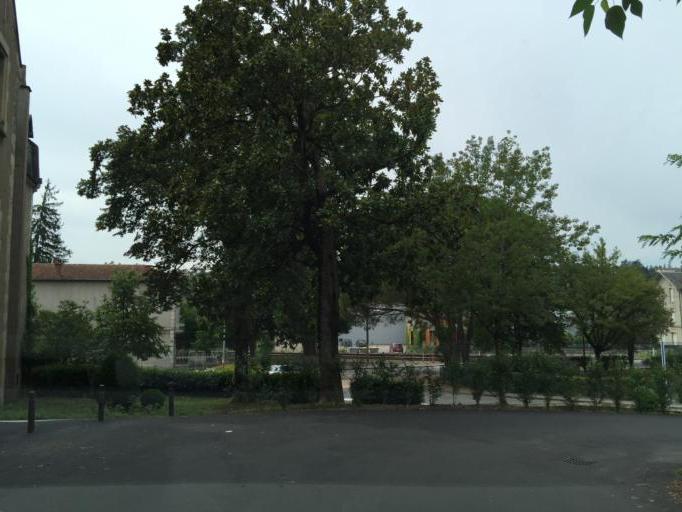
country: FR
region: Midi-Pyrenees
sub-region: Departement de l'Aveyron
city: Villefranche-de-Rouergue
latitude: 44.3447
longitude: 2.0333
